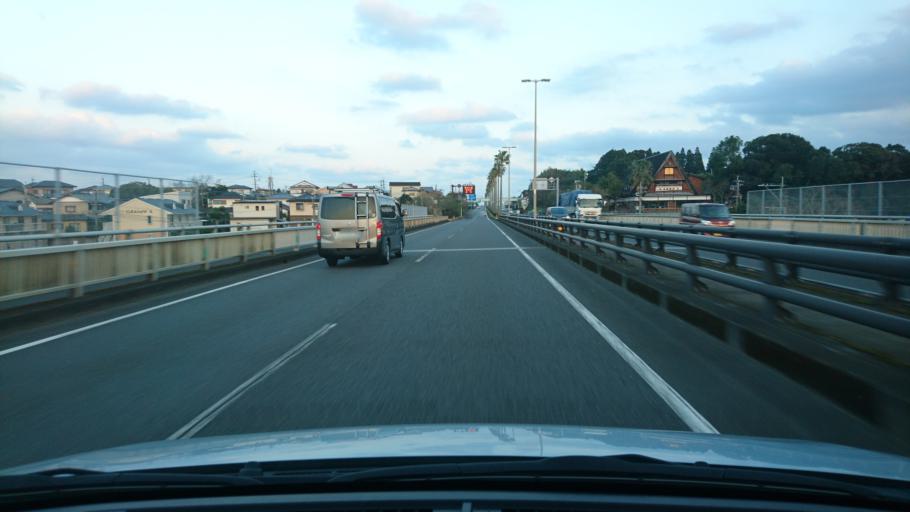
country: JP
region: Miyazaki
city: Miyazaki-shi
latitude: 31.8683
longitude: 131.4231
